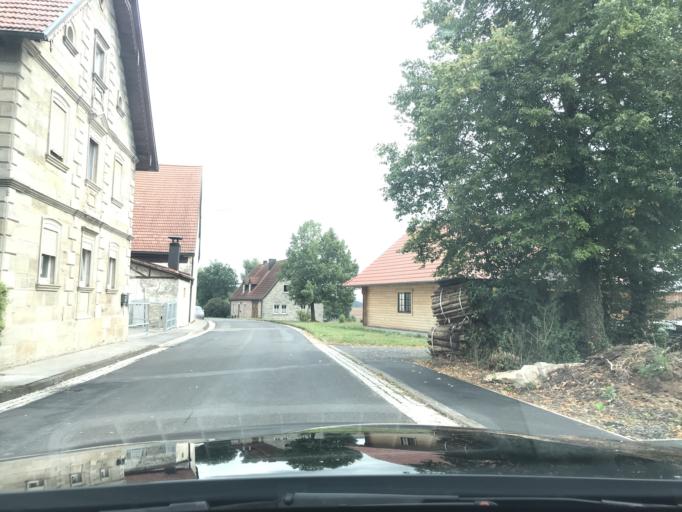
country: DE
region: Bavaria
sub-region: Regierungsbezirk Unterfranken
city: Kirchlauter
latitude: 50.0619
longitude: 10.6732
